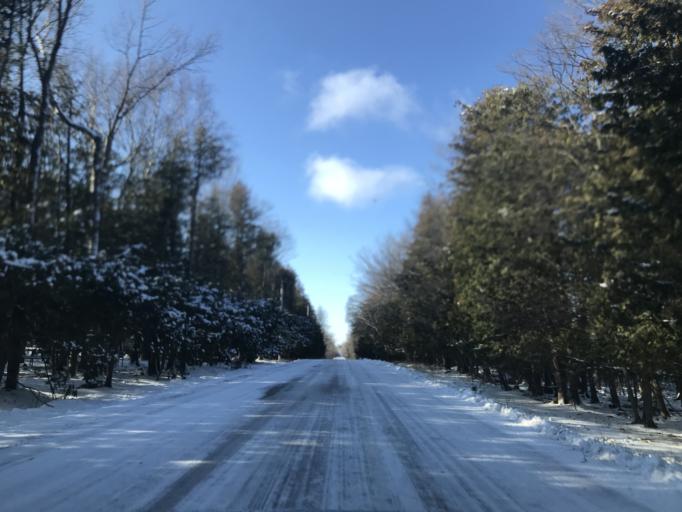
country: US
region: Wisconsin
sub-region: Door County
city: Sturgeon Bay
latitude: 44.8494
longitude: -87.4998
